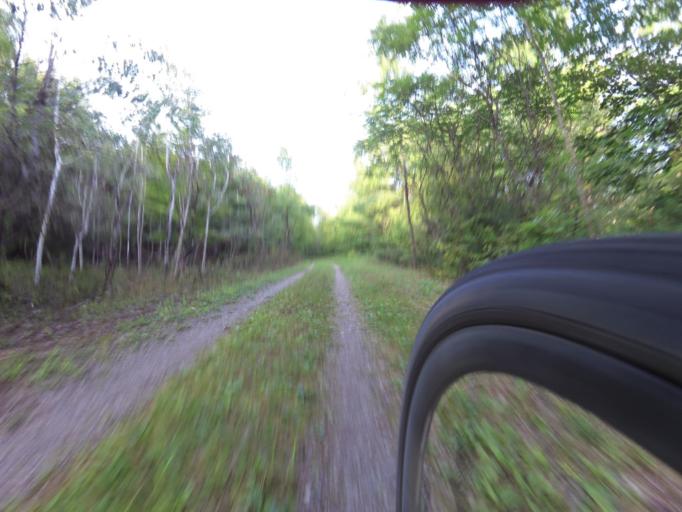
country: CA
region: Ontario
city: Gananoque
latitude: 44.5748
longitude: -76.3377
